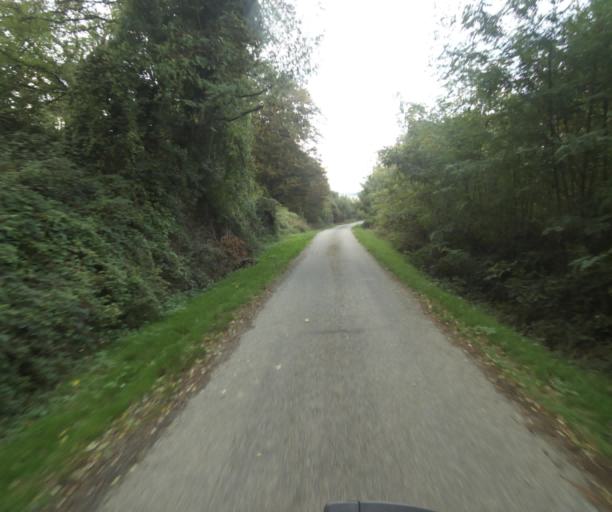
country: FR
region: Midi-Pyrenees
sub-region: Departement de la Haute-Garonne
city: Launac
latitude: 43.8155
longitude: 1.0940
